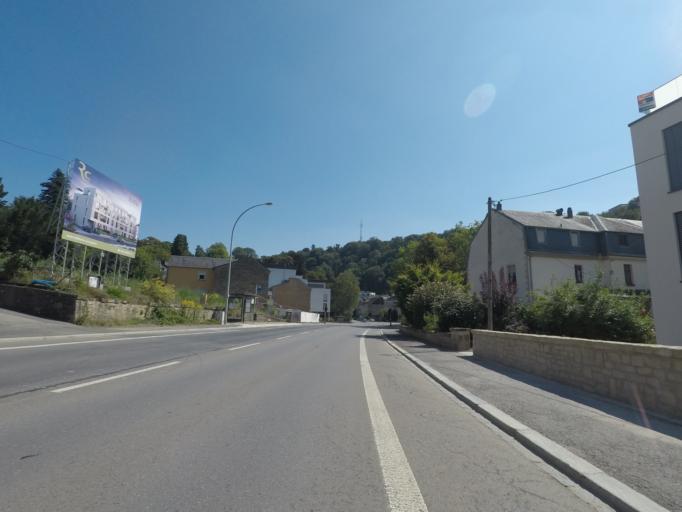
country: LU
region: Luxembourg
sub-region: Canton de Luxembourg
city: Luxembourg
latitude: 49.6284
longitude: 6.1217
